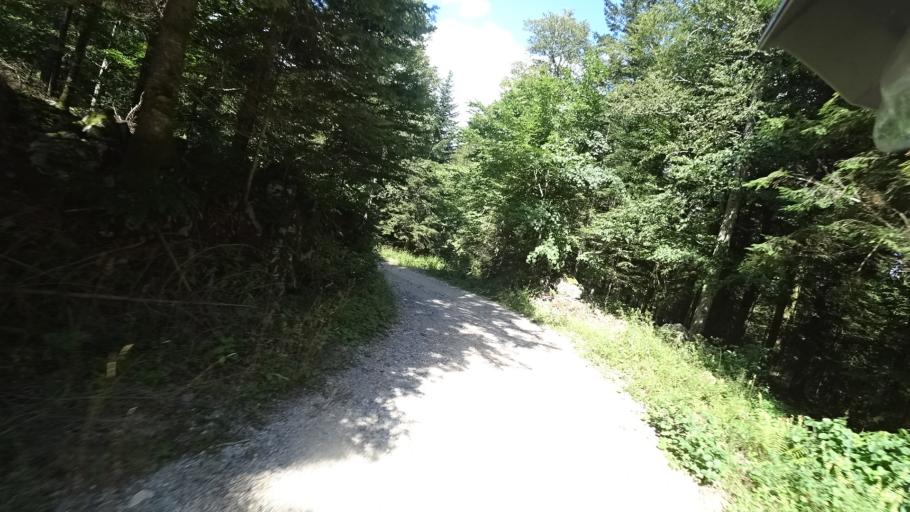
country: BA
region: Federation of Bosnia and Herzegovina
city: Orasac
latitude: 44.5058
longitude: 15.9283
